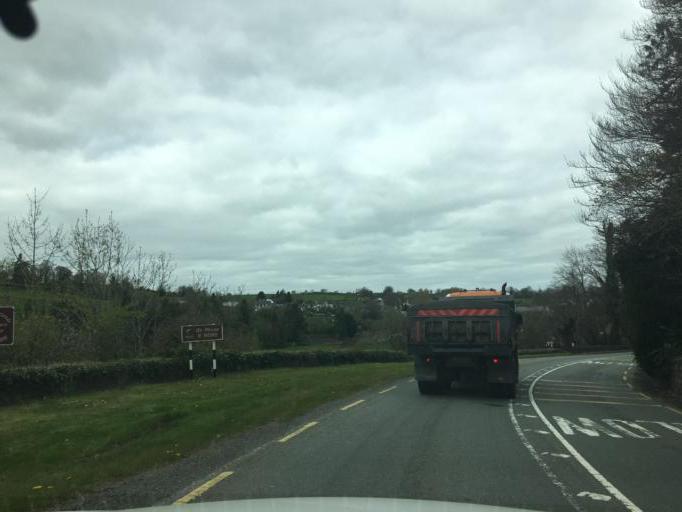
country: IE
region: Leinster
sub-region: Kilkenny
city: Thomastown
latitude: 52.4852
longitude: -7.0619
